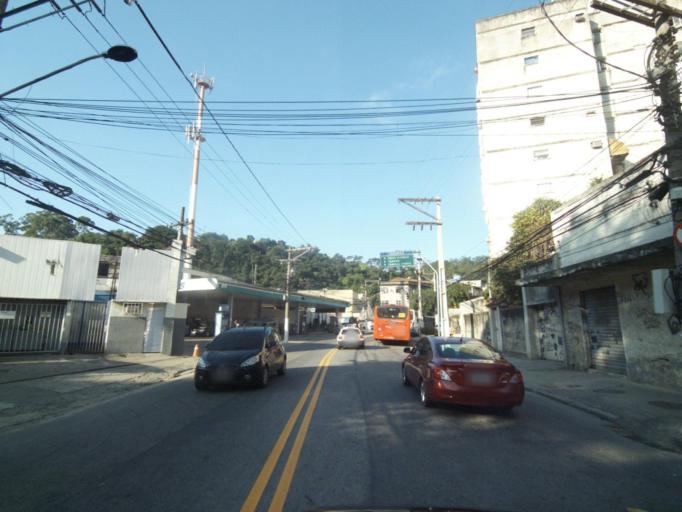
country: BR
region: Rio de Janeiro
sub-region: Niteroi
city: Niteroi
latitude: -22.8897
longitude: -43.0963
